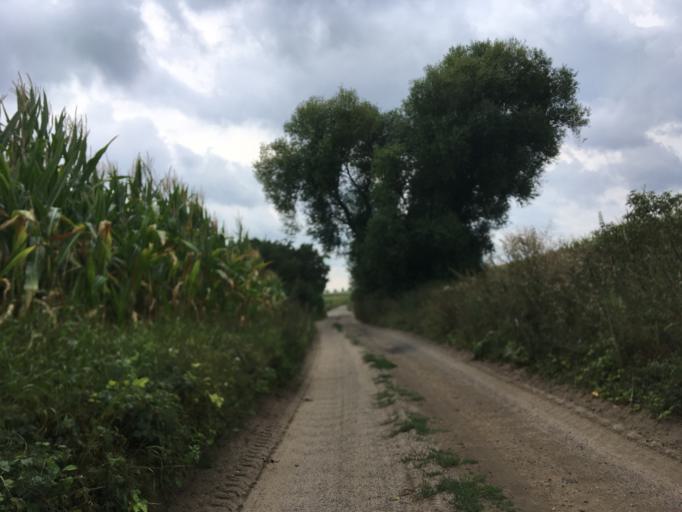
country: DE
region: Brandenburg
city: Angermunde
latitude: 52.9765
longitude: 13.9528
